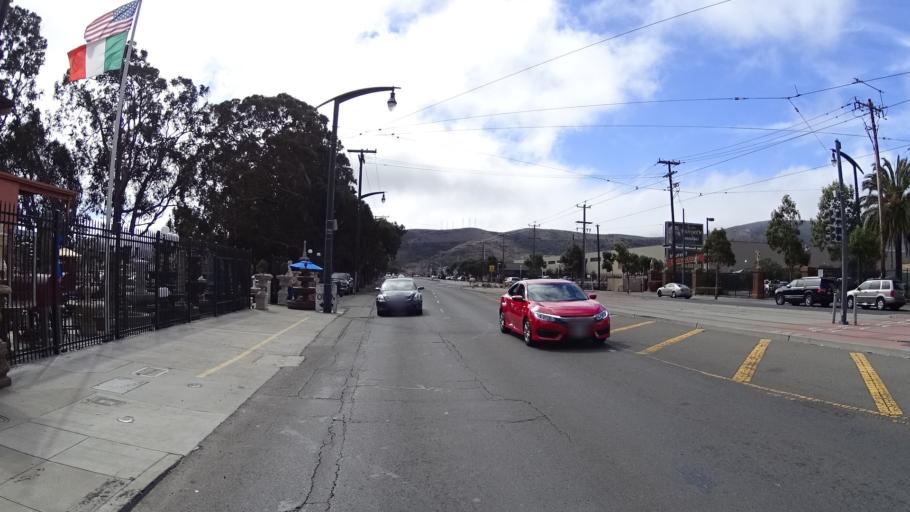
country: US
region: California
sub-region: San Mateo County
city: Brisbane
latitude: 37.7083
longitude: -122.4052
